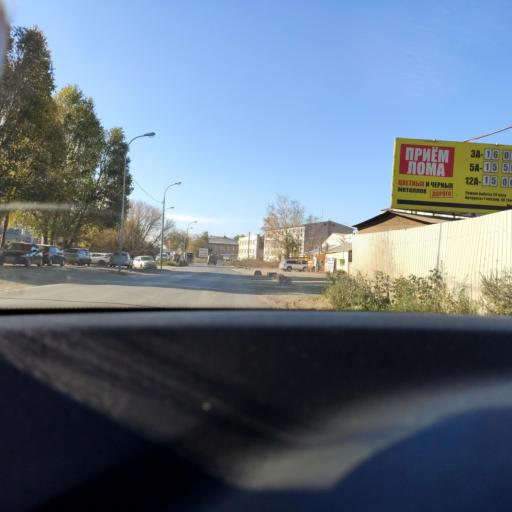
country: RU
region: Samara
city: Petra-Dubrava
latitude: 53.2473
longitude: 50.3050
